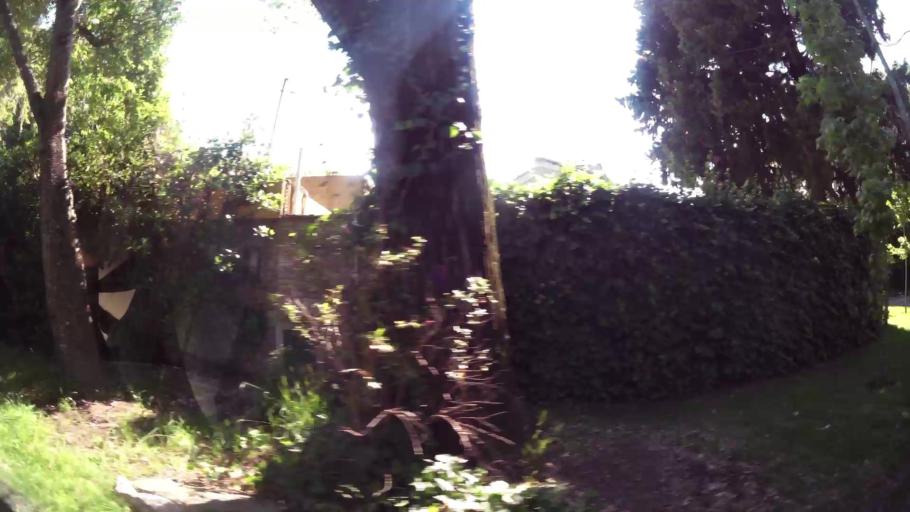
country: AR
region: Buenos Aires
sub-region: Partido de Tigre
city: Tigre
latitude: -34.4779
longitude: -58.5753
